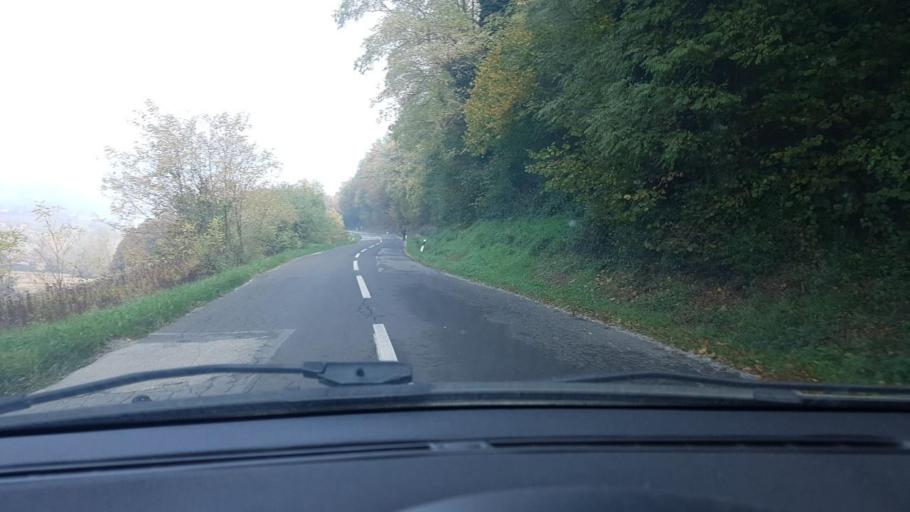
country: HR
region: Krapinsko-Zagorska
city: Zlatar
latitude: 46.1328
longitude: 16.1339
